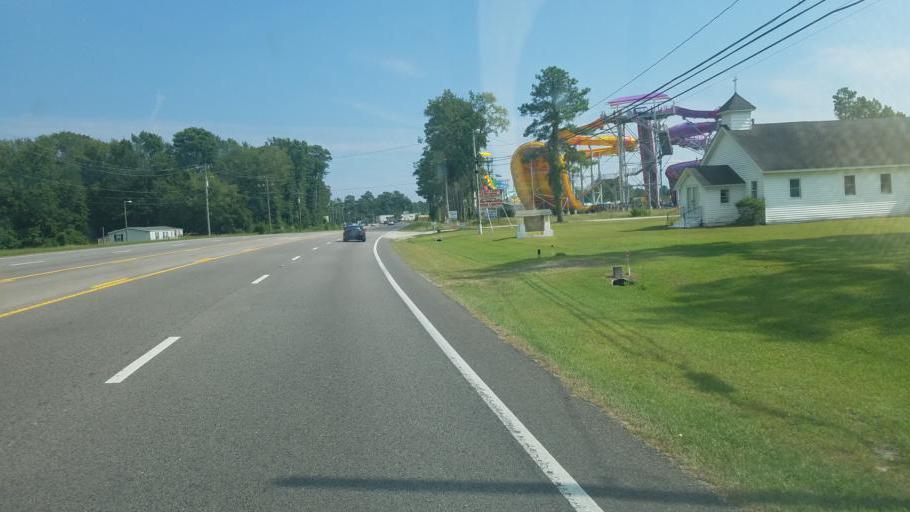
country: US
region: North Carolina
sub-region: Dare County
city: Southern Shores
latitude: 36.1143
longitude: -75.8280
